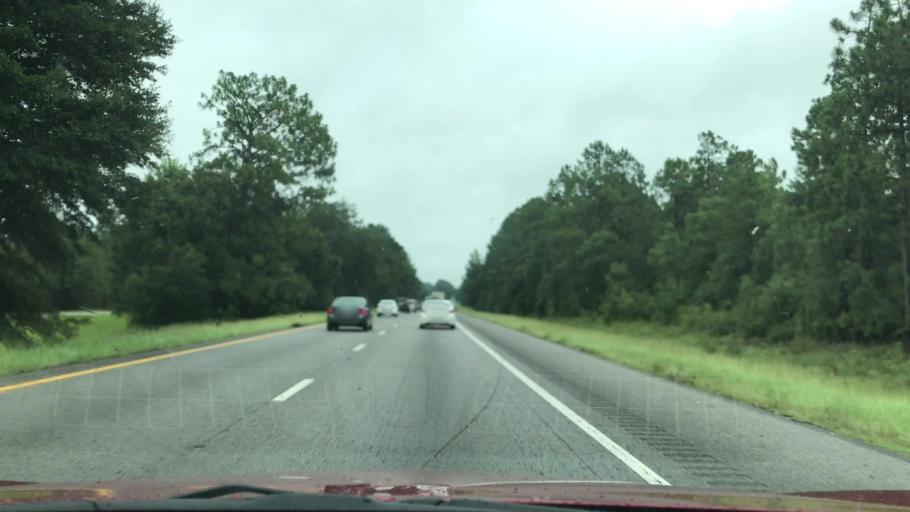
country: US
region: South Carolina
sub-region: Dorchester County
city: Ridgeville
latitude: 33.1711
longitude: -80.3660
